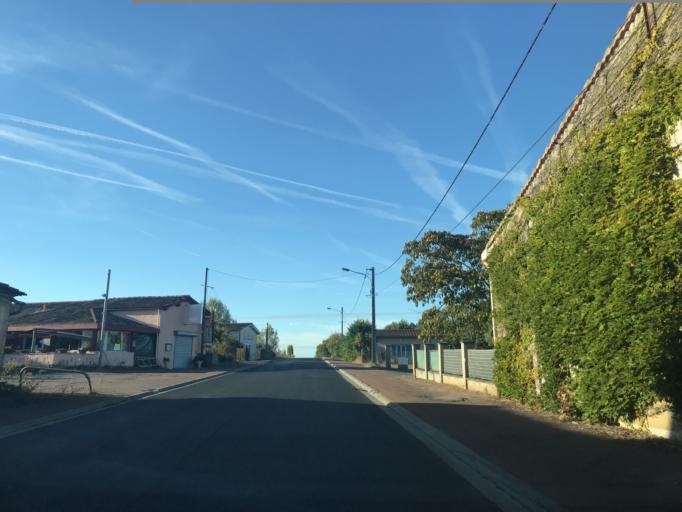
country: FR
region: Poitou-Charentes
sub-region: Departement de la Charente-Maritime
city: Montguyon
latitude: 45.1901
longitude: -0.1374
